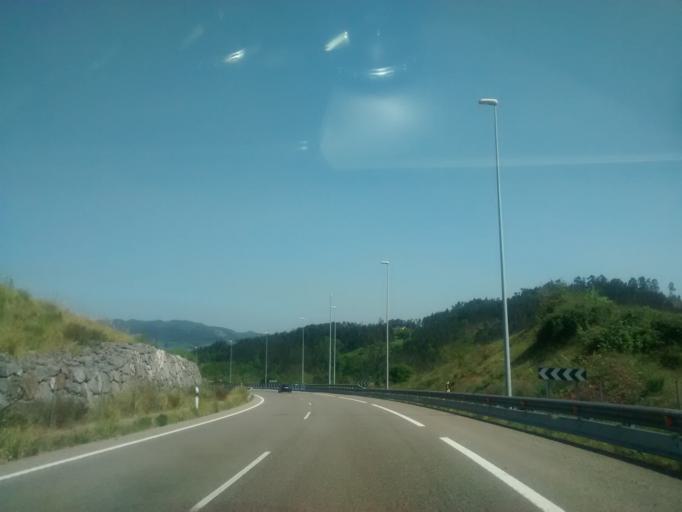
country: ES
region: Asturias
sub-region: Province of Asturias
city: Villaviciosa
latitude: 43.4646
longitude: -5.4898
